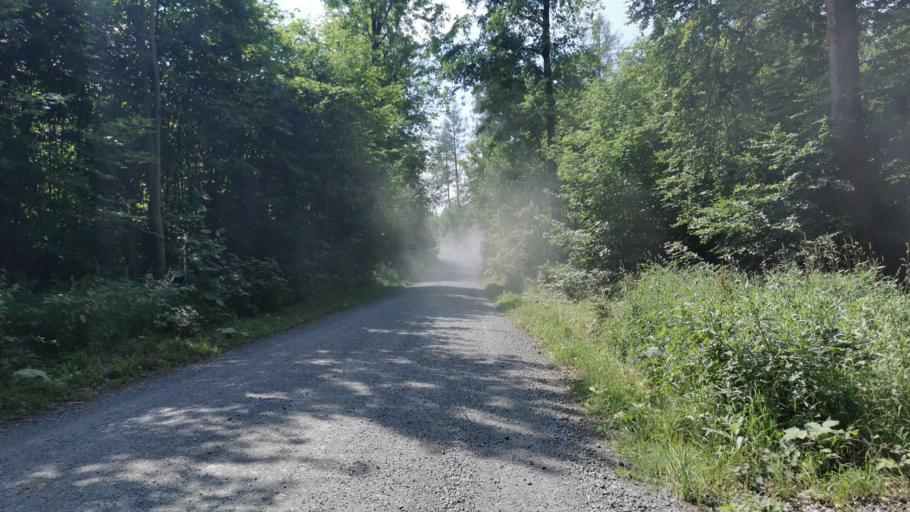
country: DE
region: Bavaria
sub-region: Upper Franconia
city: Wilhelmsthal
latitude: 50.2958
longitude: 11.3988
